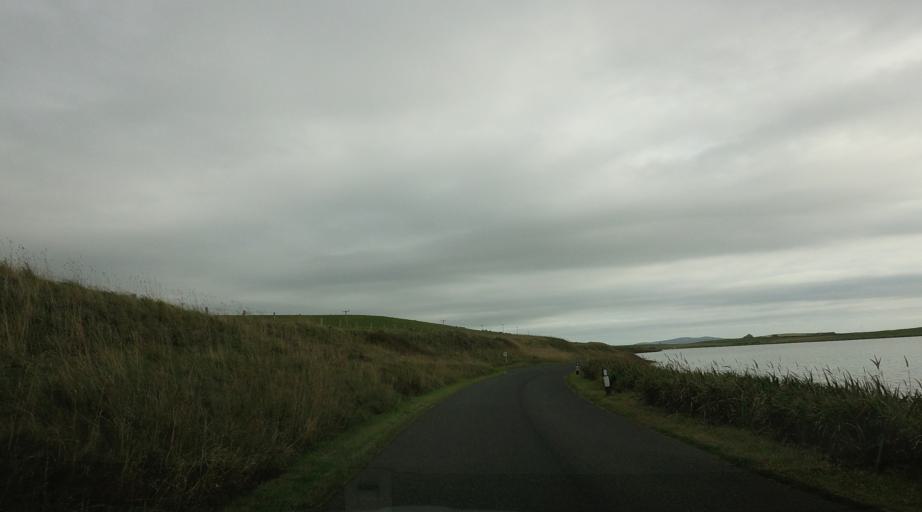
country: GB
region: Scotland
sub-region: Orkney Islands
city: Stromness
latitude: 59.0474
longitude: -3.3238
